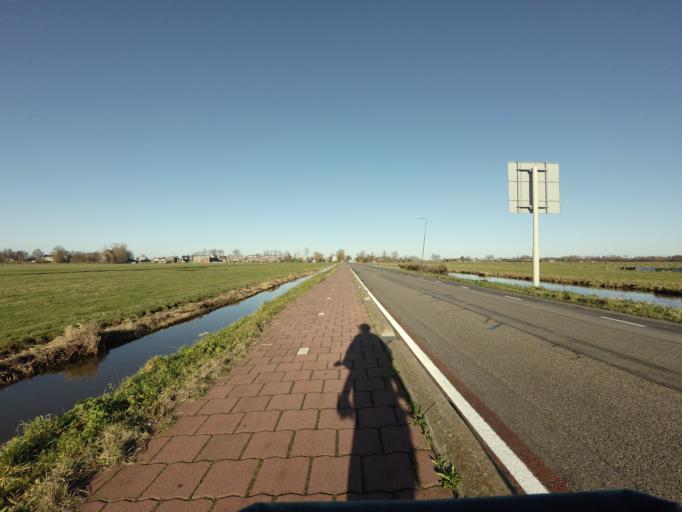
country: NL
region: Utrecht
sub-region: Gemeente De Ronde Venen
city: Mijdrecht
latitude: 52.2179
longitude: 4.9042
